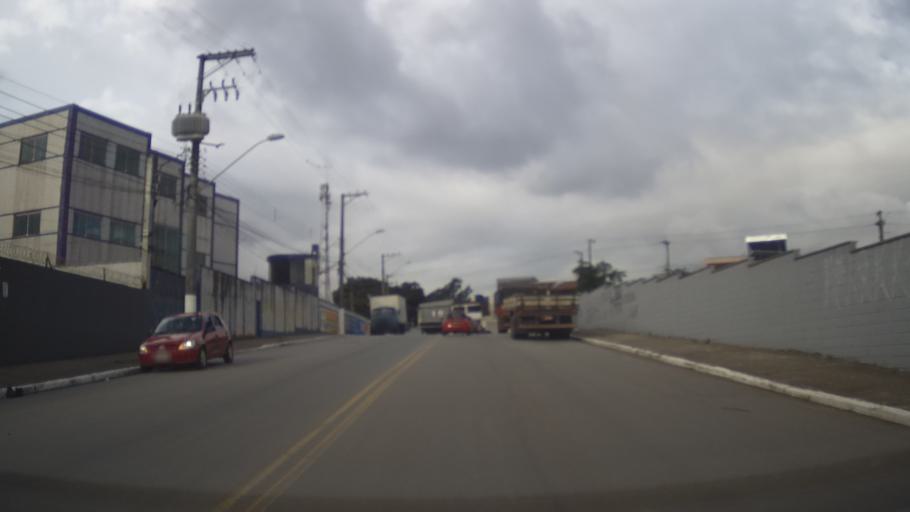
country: BR
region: Sao Paulo
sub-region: Itaquaquecetuba
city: Itaquaquecetuba
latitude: -23.4537
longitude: -46.4248
